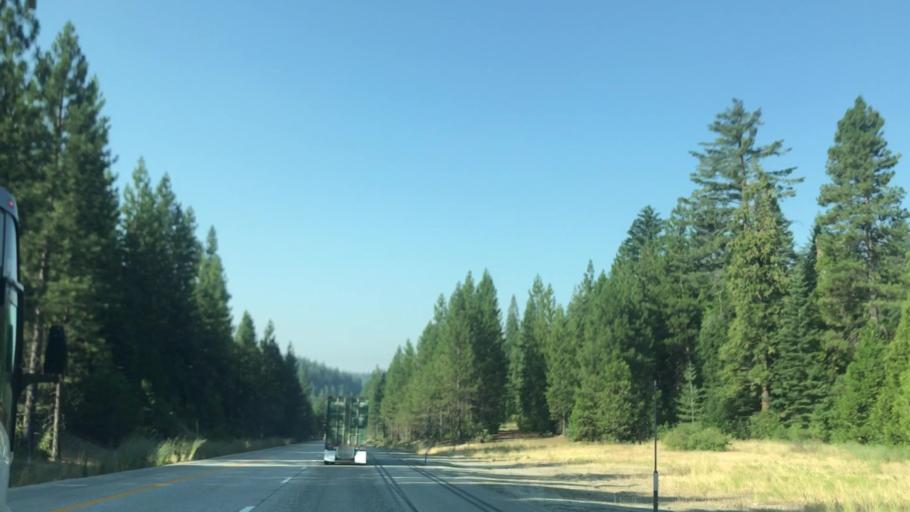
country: US
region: California
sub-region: Placer County
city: Foresthill
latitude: 39.2615
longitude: -120.7308
